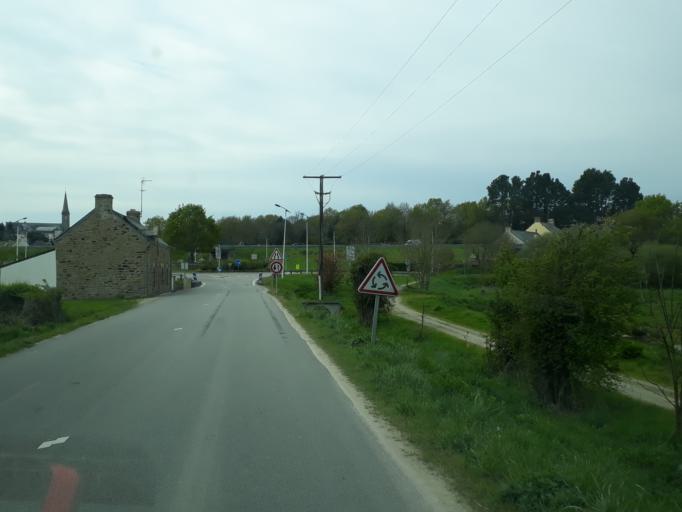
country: FR
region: Brittany
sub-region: Departement du Morbihan
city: Theix
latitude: 47.6336
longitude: -2.6479
